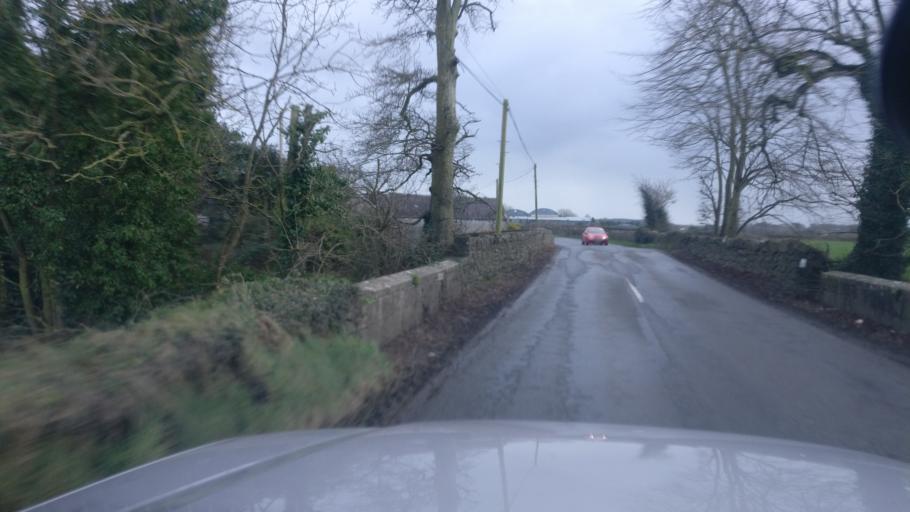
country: IE
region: Munster
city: Nenagh Bridge
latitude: 52.9847
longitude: -8.1072
